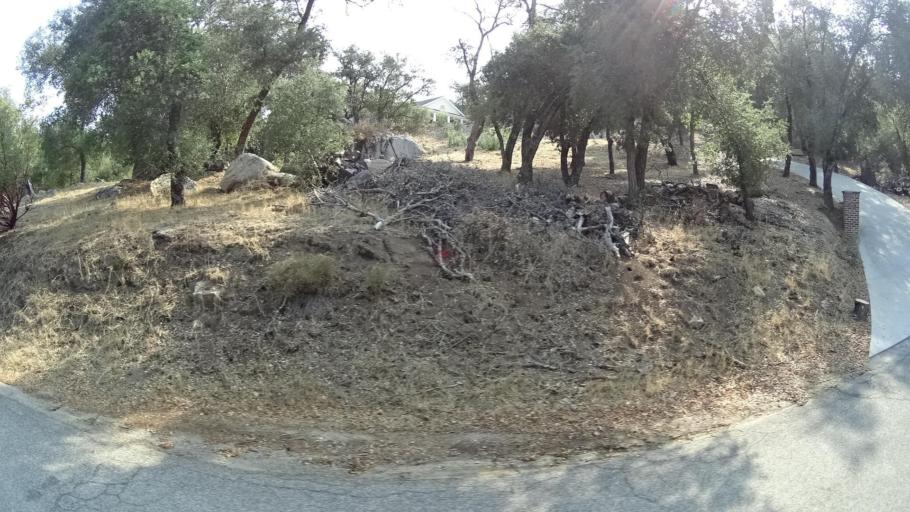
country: US
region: California
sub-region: San Diego County
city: Julian
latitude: 33.1034
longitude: -116.6580
